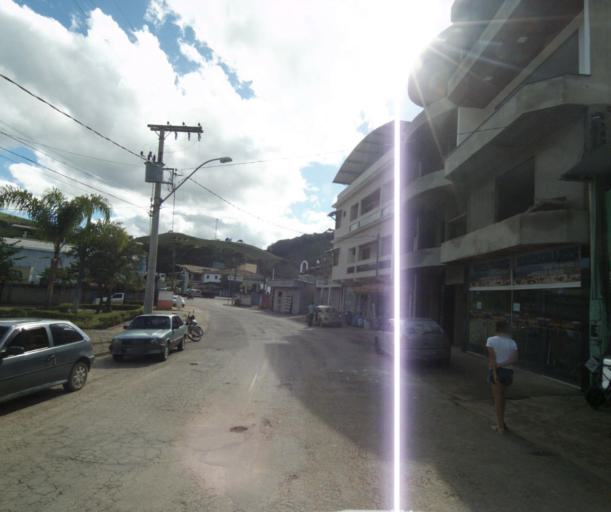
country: BR
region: Espirito Santo
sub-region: Irupi
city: Irupi
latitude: -20.5383
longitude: -41.6641
